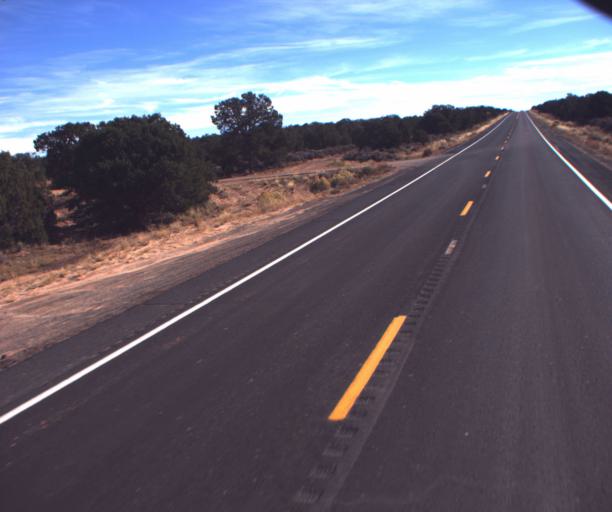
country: US
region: Arizona
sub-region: Coconino County
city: Kaibito
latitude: 36.5899
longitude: -110.8817
